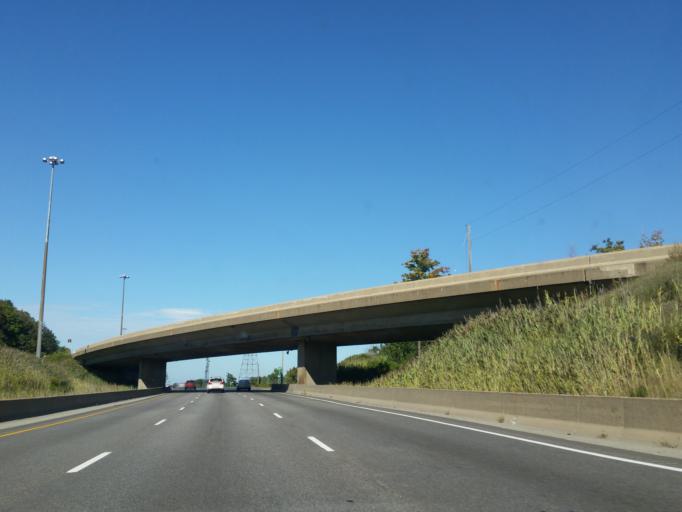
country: CA
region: Ontario
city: Thorold
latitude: 43.1514
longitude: -79.1490
